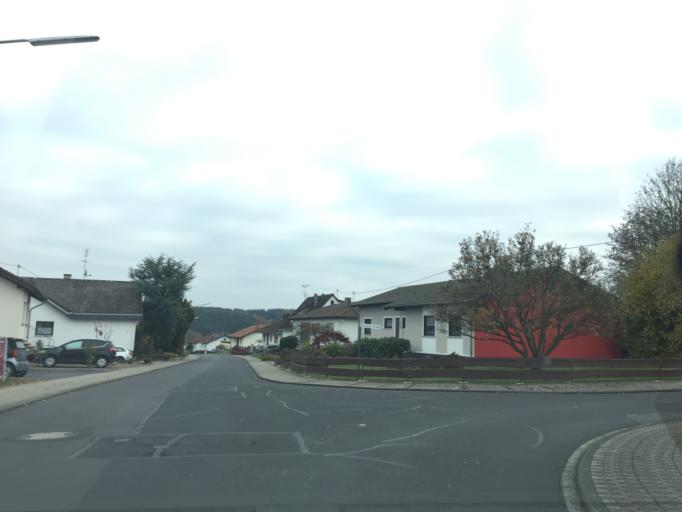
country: DE
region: Rheinland-Pfalz
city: Heiligenroth
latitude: 50.4469
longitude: 7.8609
